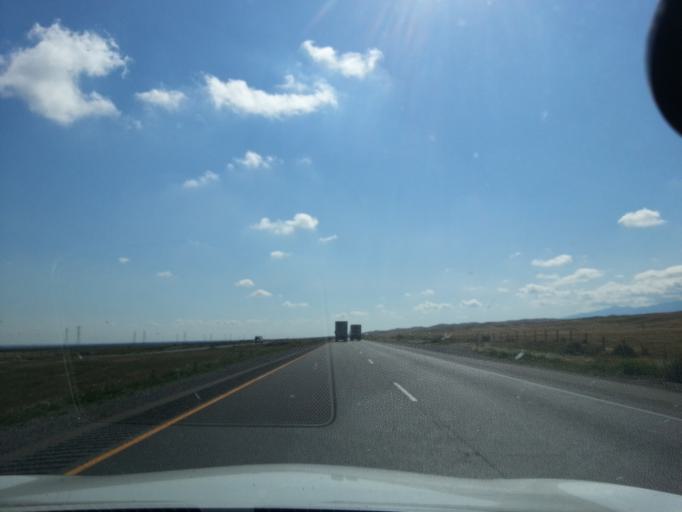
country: US
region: California
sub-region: Fresno County
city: Mendota
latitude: 36.5108
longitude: -120.4648
